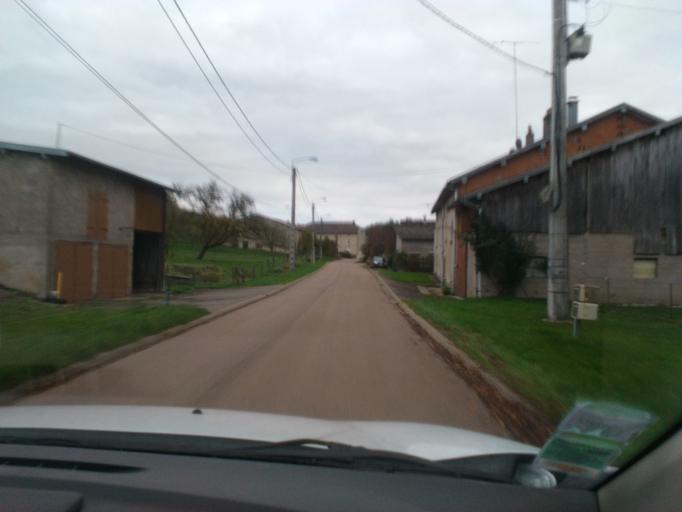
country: FR
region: Lorraine
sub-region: Departement des Vosges
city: Vincey
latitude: 48.2677
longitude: 6.2683
